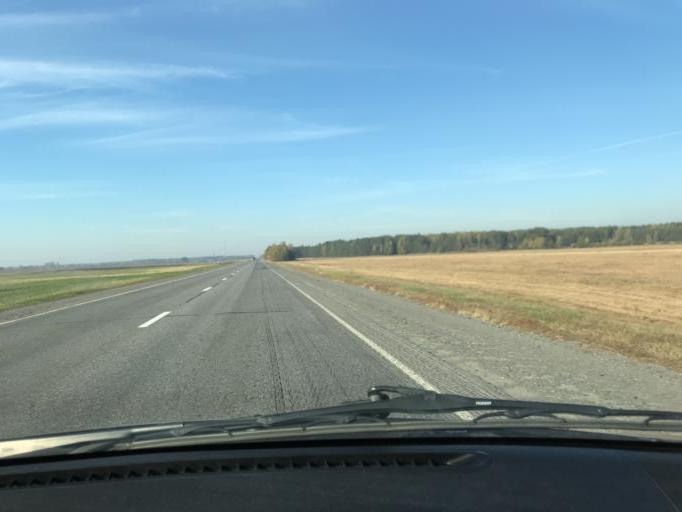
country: BY
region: Brest
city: Davyd-Haradok
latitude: 52.2428
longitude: 27.1763
